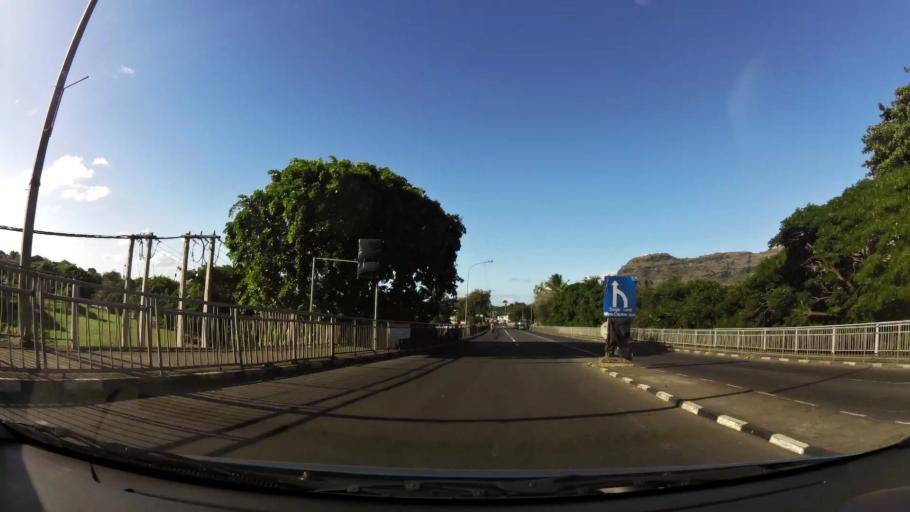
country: MU
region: Moka
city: Pailles
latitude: -20.1754
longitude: 57.4714
